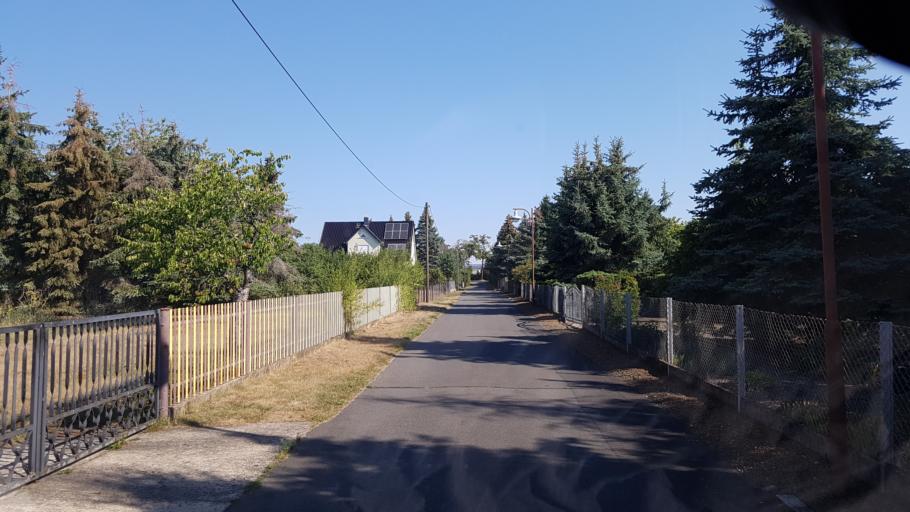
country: DE
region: Brandenburg
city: Plessa
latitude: 51.4716
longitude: 13.6014
